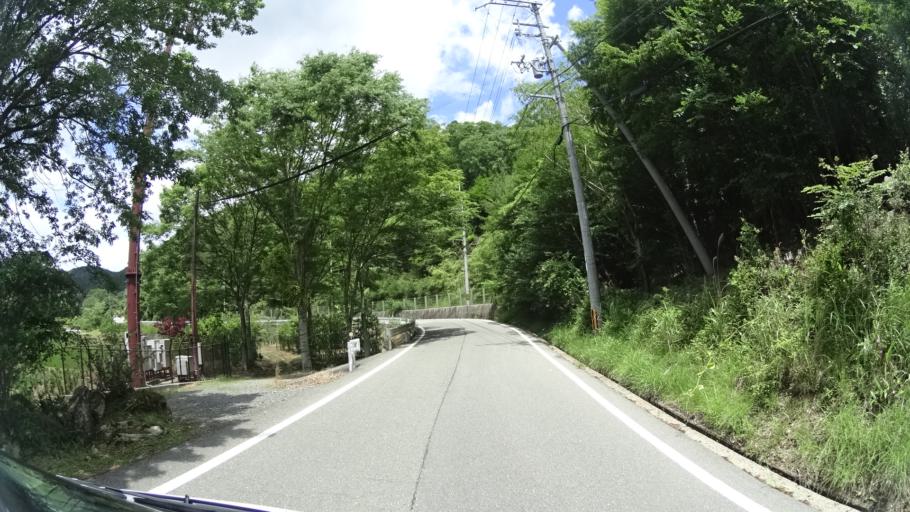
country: JP
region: Hyogo
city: Sasayama
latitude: 35.0214
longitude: 135.3958
